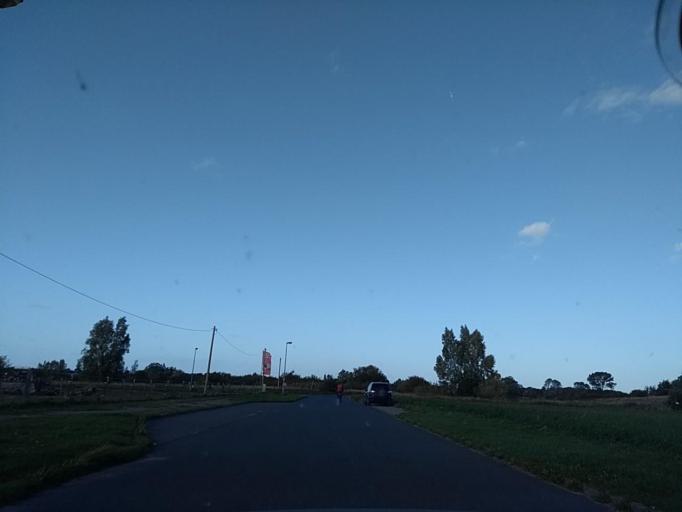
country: DE
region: Mecklenburg-Vorpommern
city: Ostseebad Dierhagen
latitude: 54.2354
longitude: 12.3693
